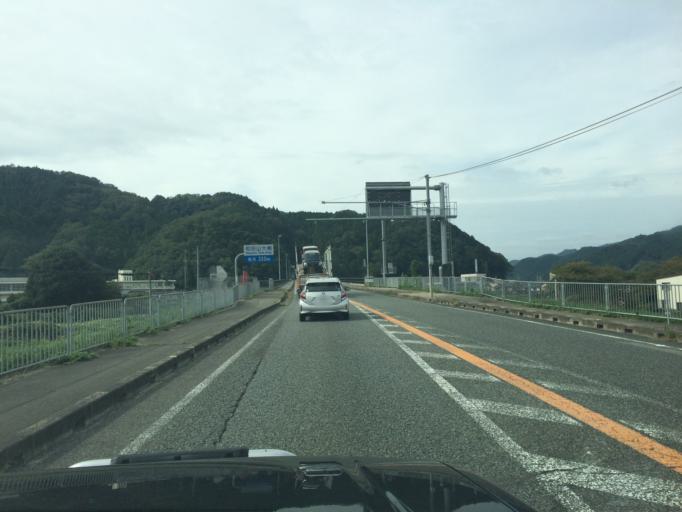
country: JP
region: Hyogo
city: Toyooka
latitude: 35.3339
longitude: 134.8600
